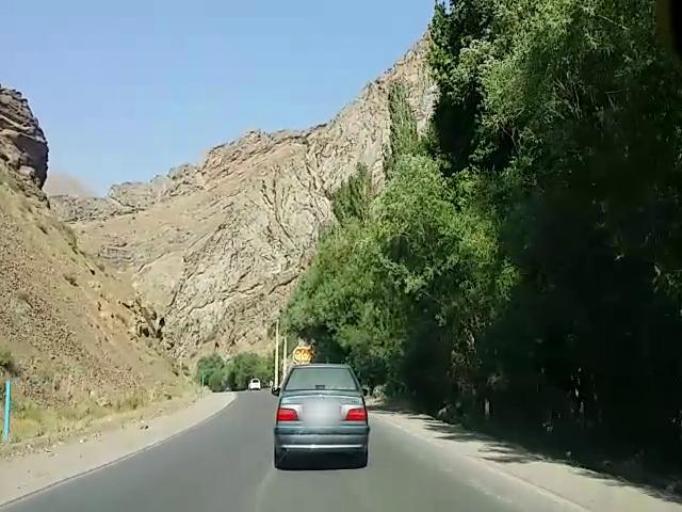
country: IR
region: Tehran
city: Tajrish
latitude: 36.0288
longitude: 51.2260
